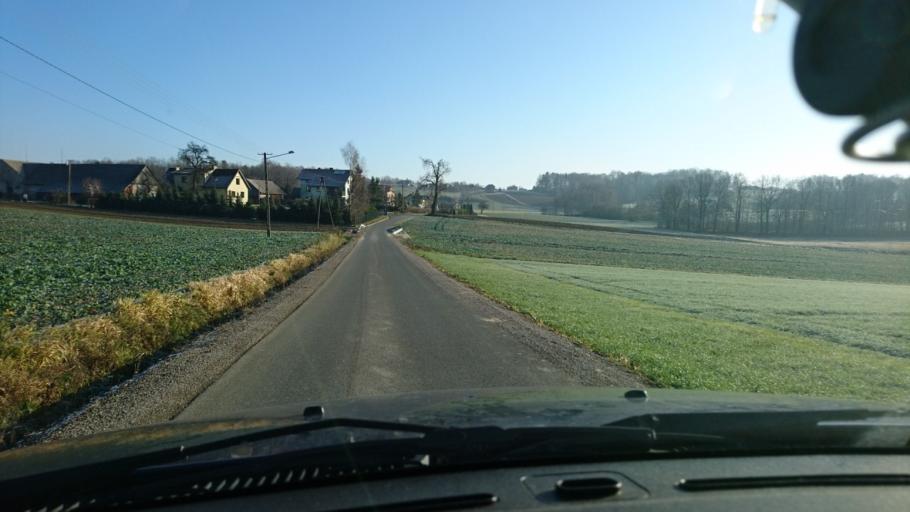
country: PL
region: Silesian Voivodeship
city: Janowice
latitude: 49.8953
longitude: 19.1043
